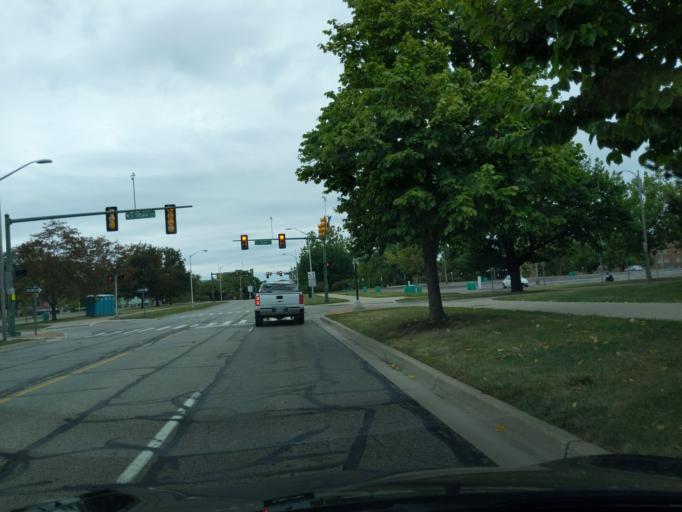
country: US
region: Michigan
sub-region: Ingham County
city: East Lansing
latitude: 42.7248
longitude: -84.4779
